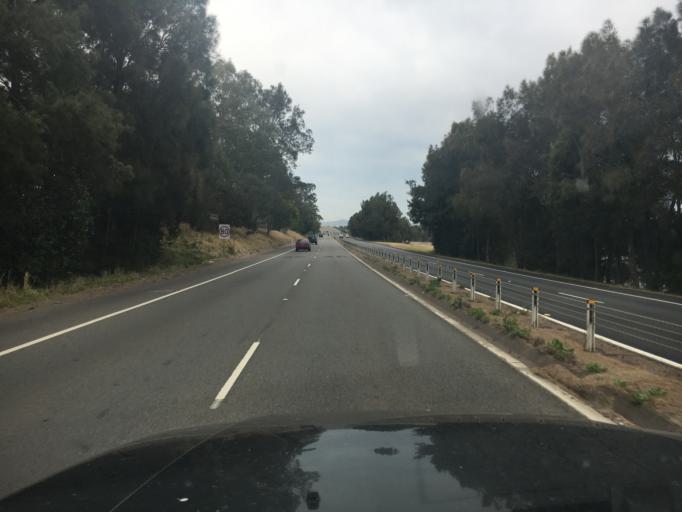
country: AU
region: New South Wales
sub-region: Maitland Municipality
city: Maitland
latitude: -32.7286
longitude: 151.5438
